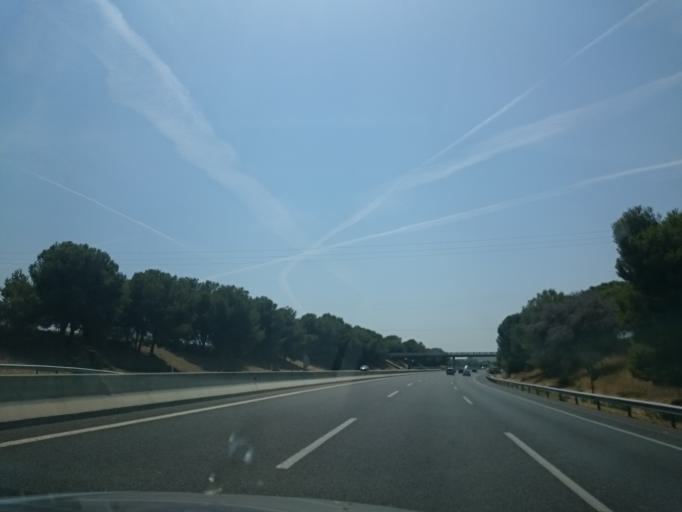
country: ES
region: Catalonia
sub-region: Provincia de Barcelona
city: Castellet
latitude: 41.3162
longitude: 1.6366
